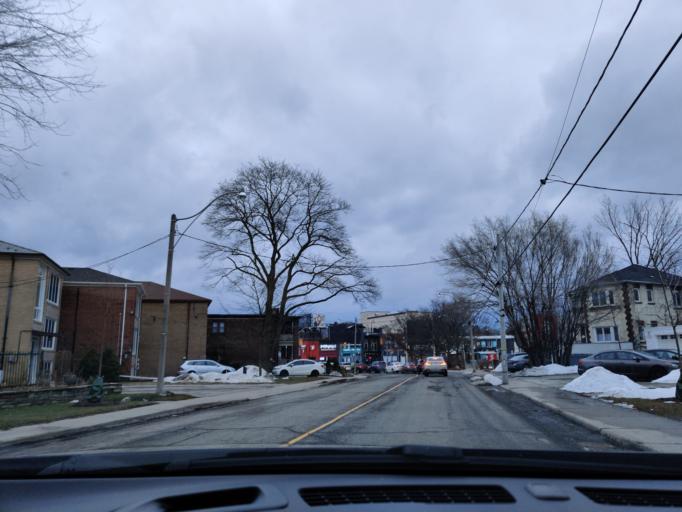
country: CA
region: Ontario
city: Willowdale
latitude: 43.7345
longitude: -79.4060
